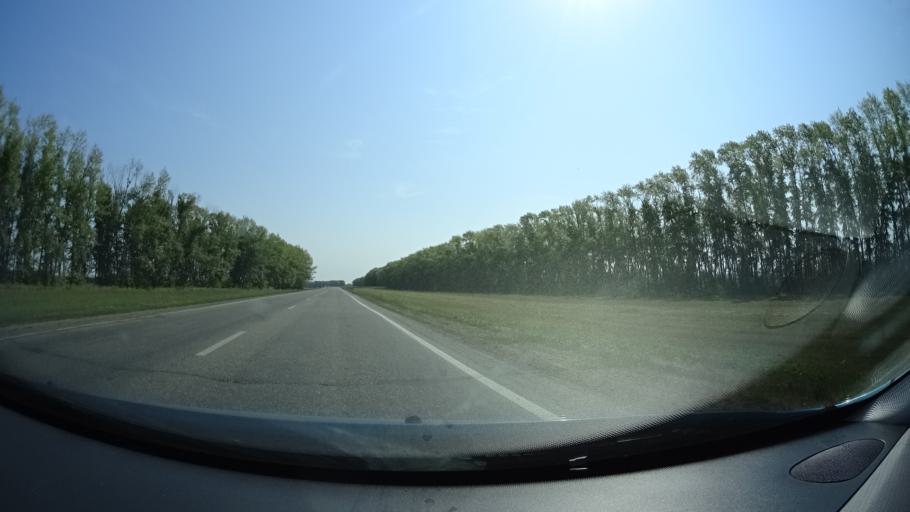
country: RU
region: Bashkortostan
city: Karmaskaly
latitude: 54.3911
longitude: 56.1217
